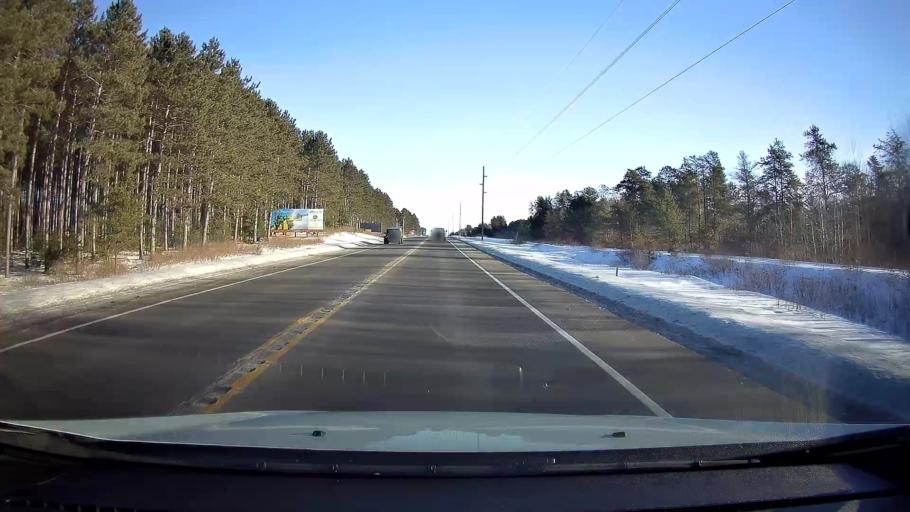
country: US
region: Wisconsin
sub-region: Sawyer County
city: Hayward
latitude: 45.9947
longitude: -91.5127
